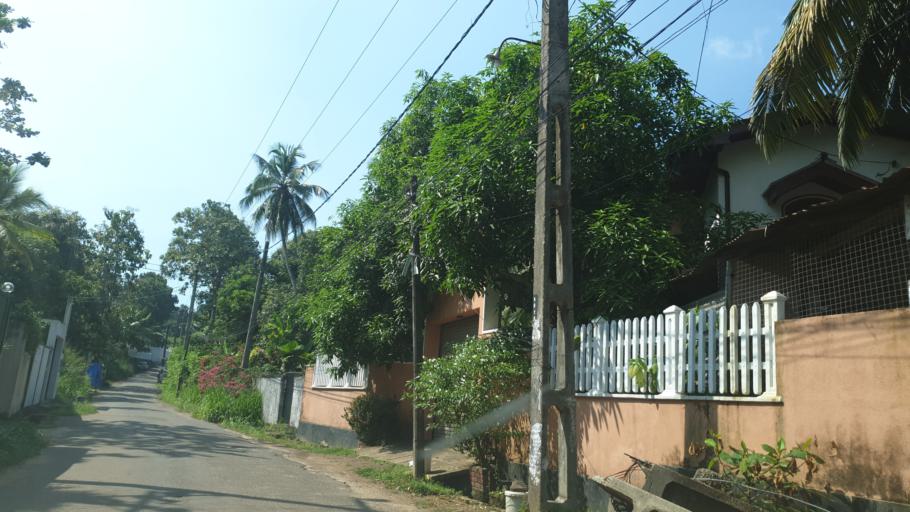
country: LK
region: Western
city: Moratuwa
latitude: 6.7672
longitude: 79.9211
